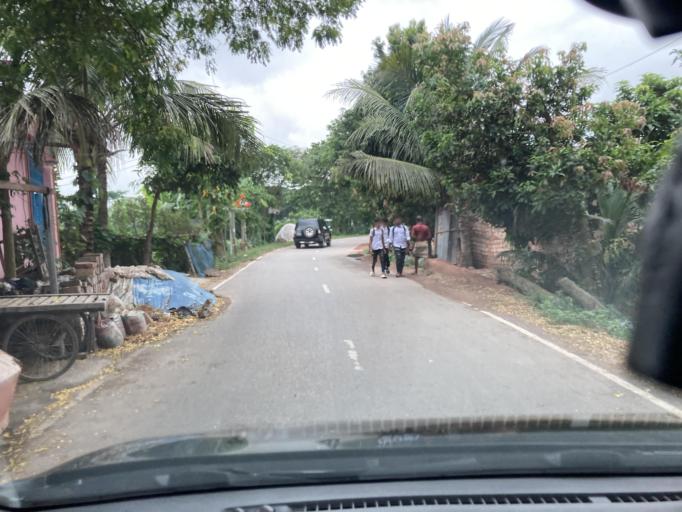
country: BD
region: Dhaka
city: Azimpur
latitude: 23.7734
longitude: 90.2055
